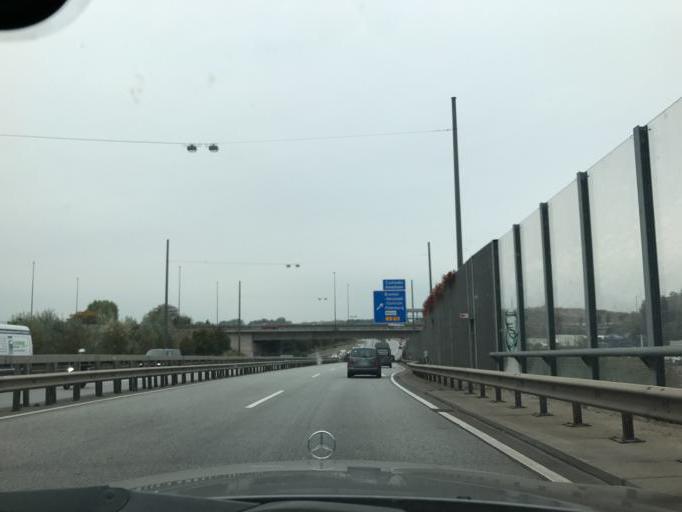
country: DE
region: Bremen
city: Bremen
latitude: 53.0651
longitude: 8.7788
